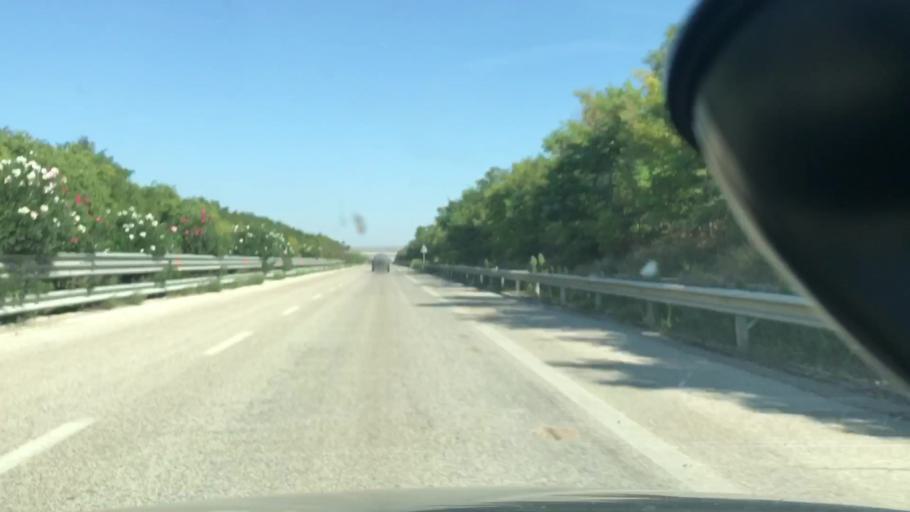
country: IT
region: Apulia
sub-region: Provincia di Foggia
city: Ordona
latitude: 41.2849
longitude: 15.5540
